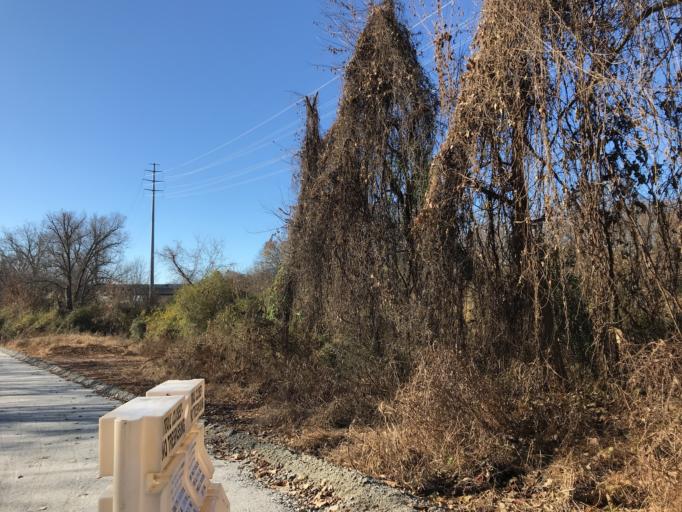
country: US
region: South Carolina
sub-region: Greenville County
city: Sans Souci
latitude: 34.8701
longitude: -82.4147
